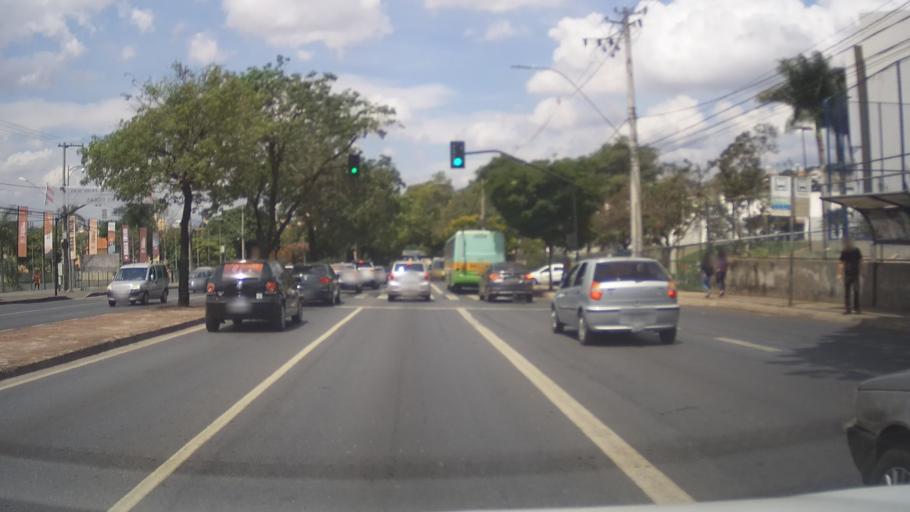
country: BR
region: Minas Gerais
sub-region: Belo Horizonte
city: Belo Horizonte
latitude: -19.9323
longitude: -43.9892
